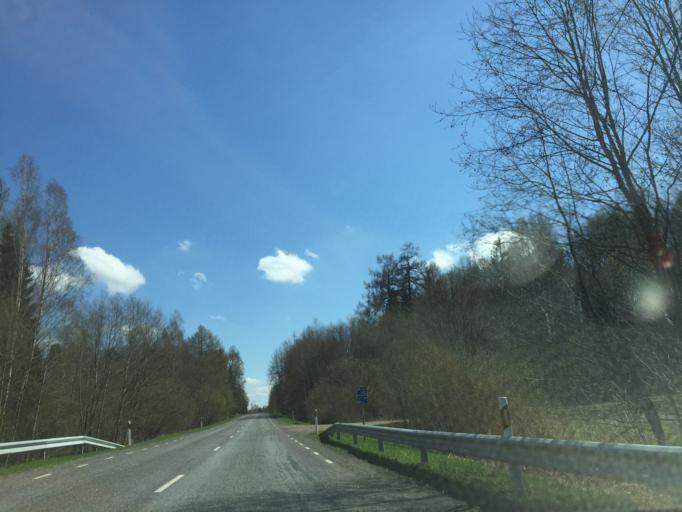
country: EE
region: Tartu
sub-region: Elva linn
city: Elva
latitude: 58.1523
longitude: 26.2238
